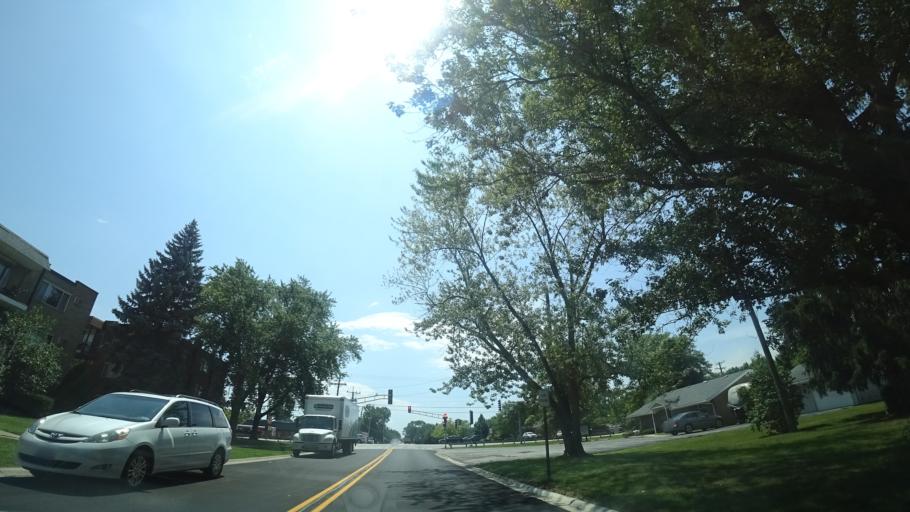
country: US
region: Illinois
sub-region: Cook County
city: Crestwood
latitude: 41.6619
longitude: -87.7582
